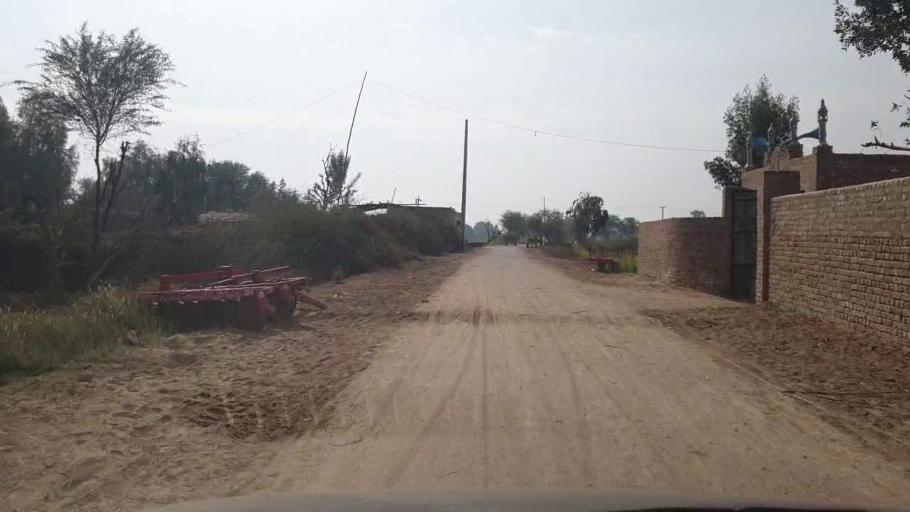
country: PK
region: Sindh
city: Hala
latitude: 25.9877
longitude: 68.4228
